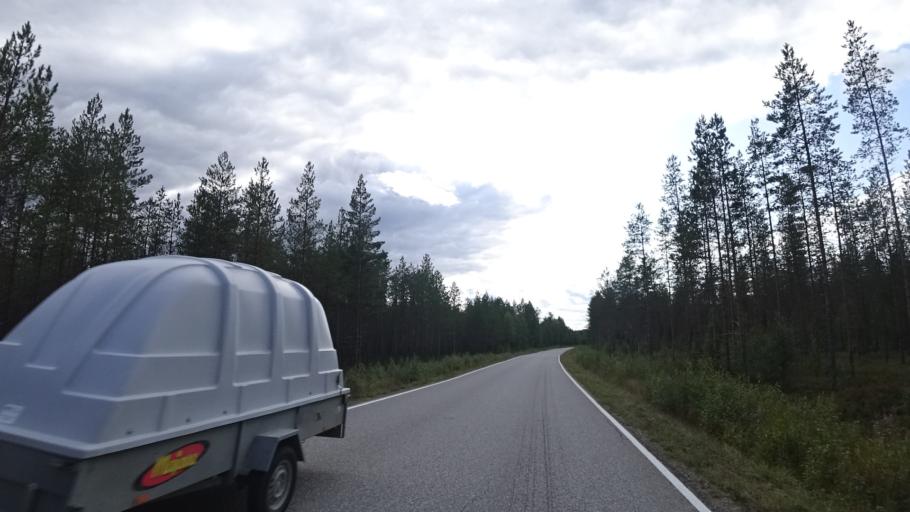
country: FI
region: North Karelia
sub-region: Joensuu
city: Ilomantsi
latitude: 62.4264
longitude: 31.0413
